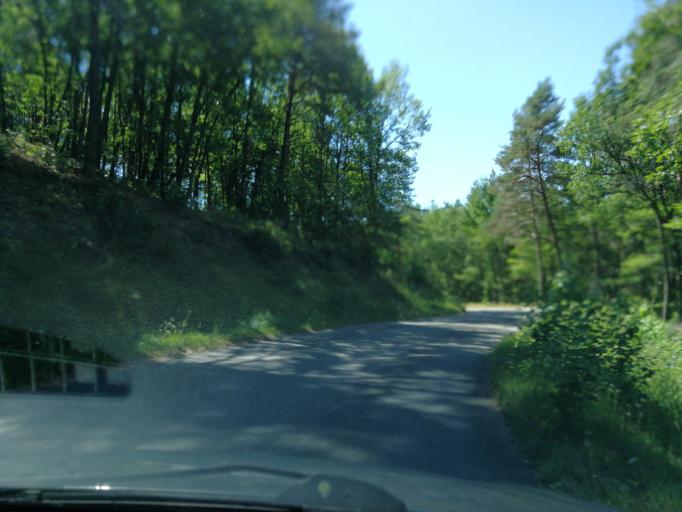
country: FR
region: Limousin
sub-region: Departement de la Correze
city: Argentat
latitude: 45.0933
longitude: 1.8989
